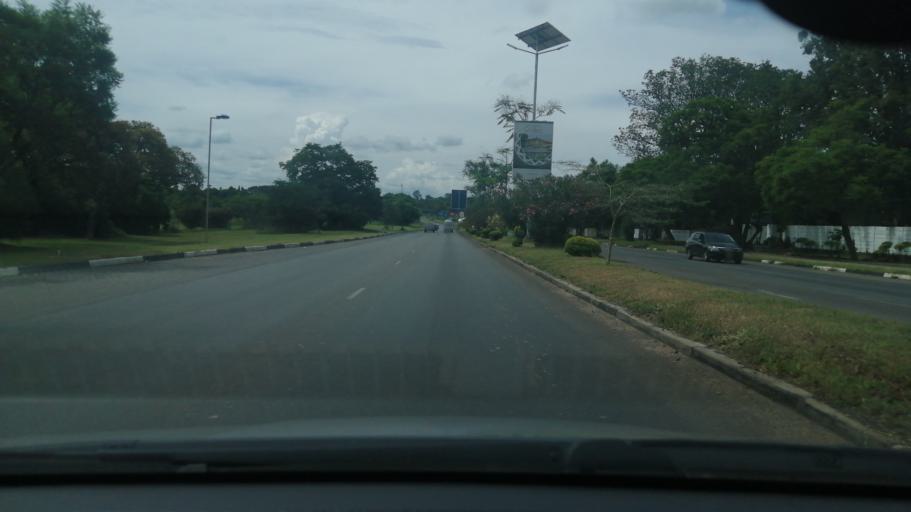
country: ZW
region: Harare
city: Harare
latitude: -17.8319
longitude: 31.1016
